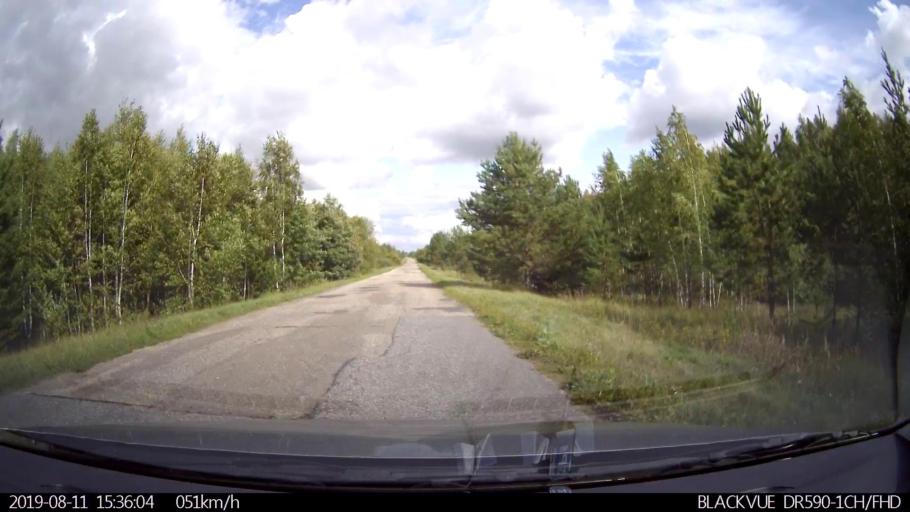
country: RU
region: Ulyanovsk
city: Ignatovka
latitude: 53.8596
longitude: 47.6158
